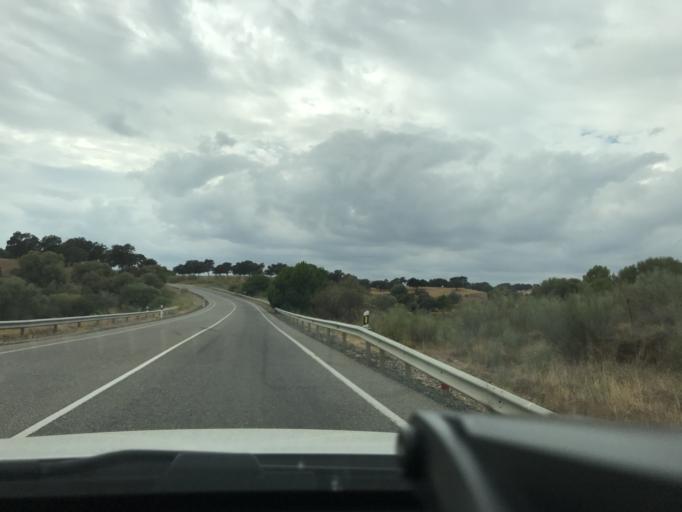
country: ES
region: Andalusia
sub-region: Provincia de Sevilla
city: Tocina
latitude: 37.6343
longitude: -5.7598
